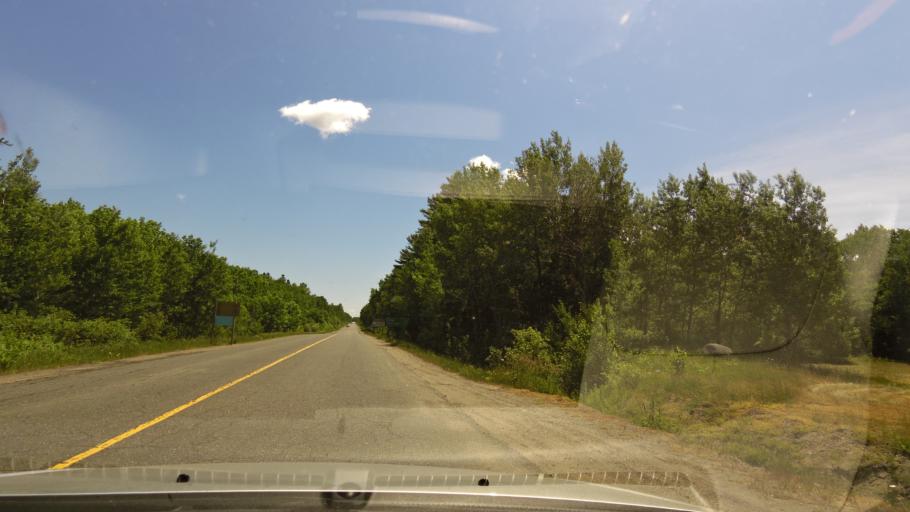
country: CA
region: Ontario
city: Greater Sudbury
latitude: 45.9135
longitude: -80.5711
